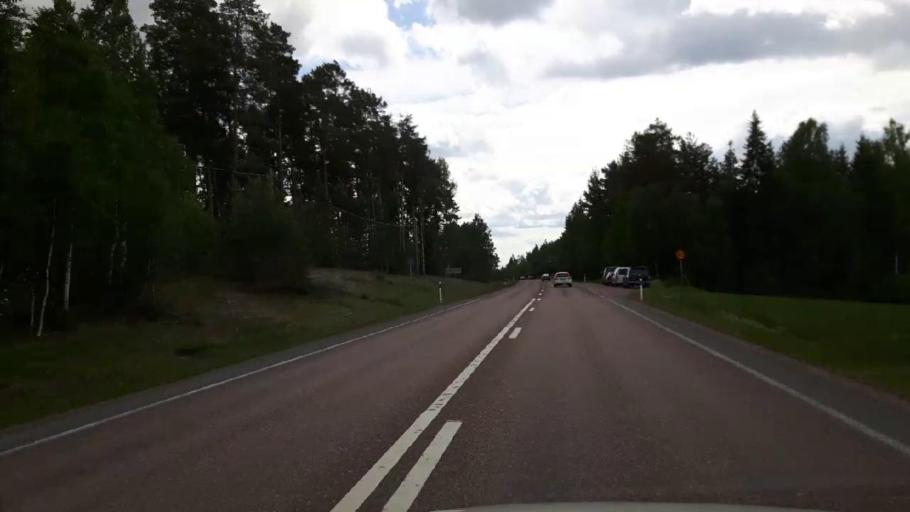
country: SE
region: Dalarna
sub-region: Saters Kommun
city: Saeter
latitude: 60.4672
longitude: 15.7981
